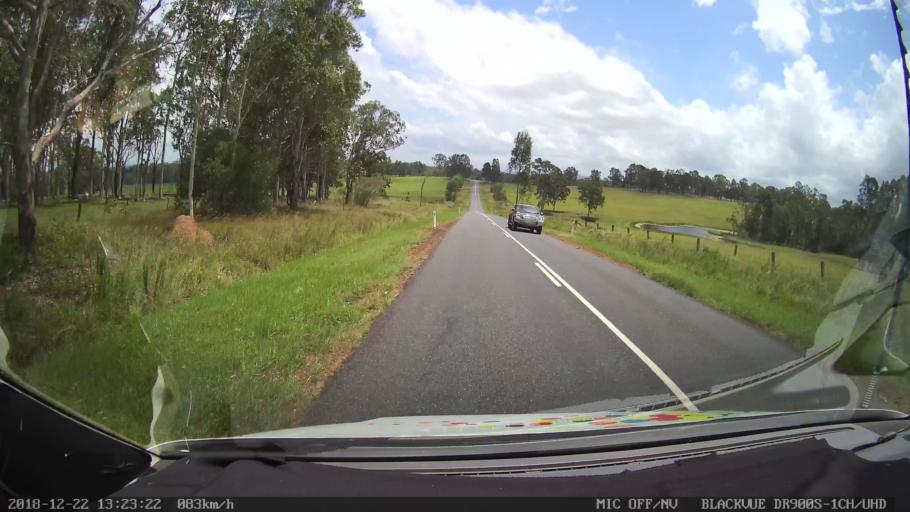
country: AU
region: New South Wales
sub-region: Clarence Valley
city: Coutts Crossing
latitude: -29.7970
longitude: 152.9075
